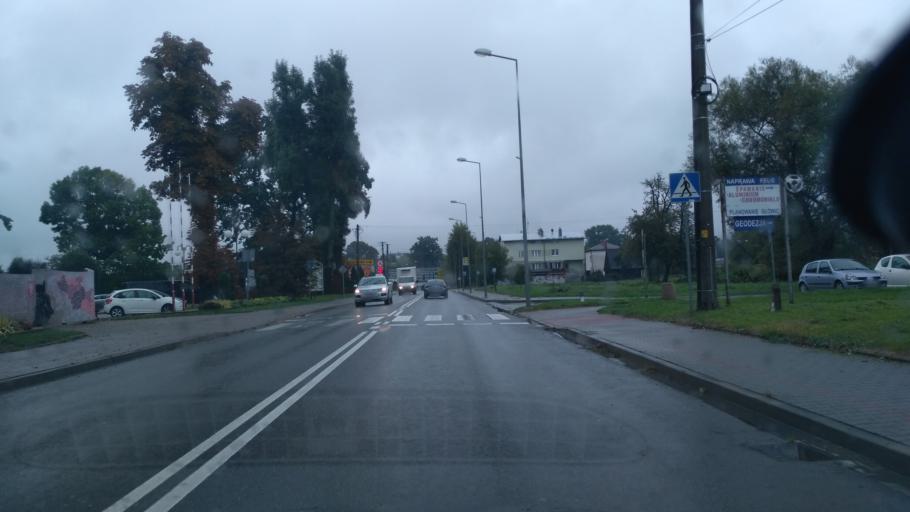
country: PL
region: Subcarpathian Voivodeship
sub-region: Powiat debicki
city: Debica
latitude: 50.0584
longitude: 21.4078
